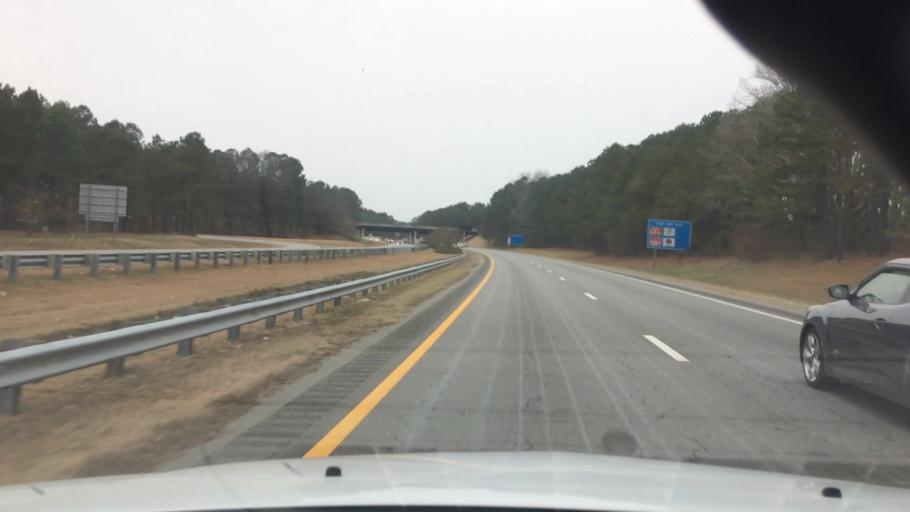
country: US
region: North Carolina
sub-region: Nash County
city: Rocky Mount
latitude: 35.9704
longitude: -77.8296
